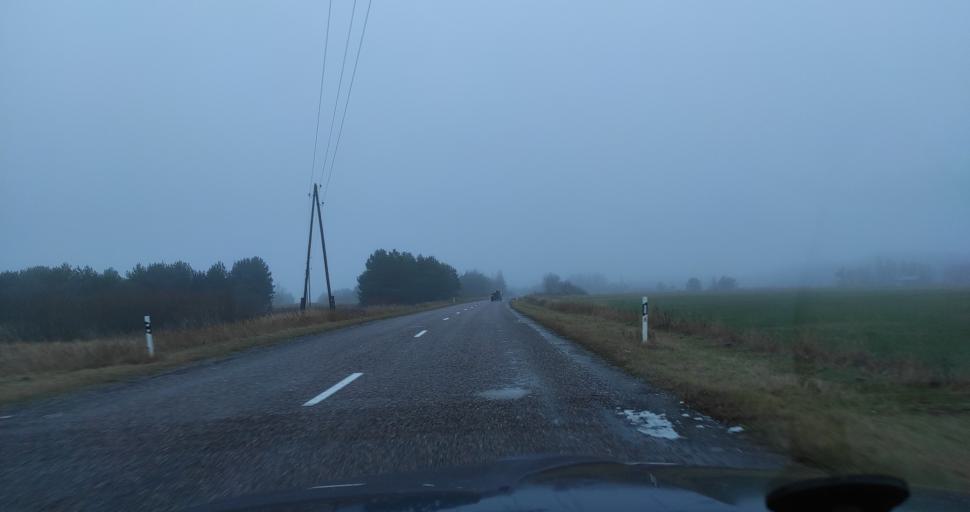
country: LV
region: Alsunga
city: Alsunga
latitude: 57.1188
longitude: 21.4246
